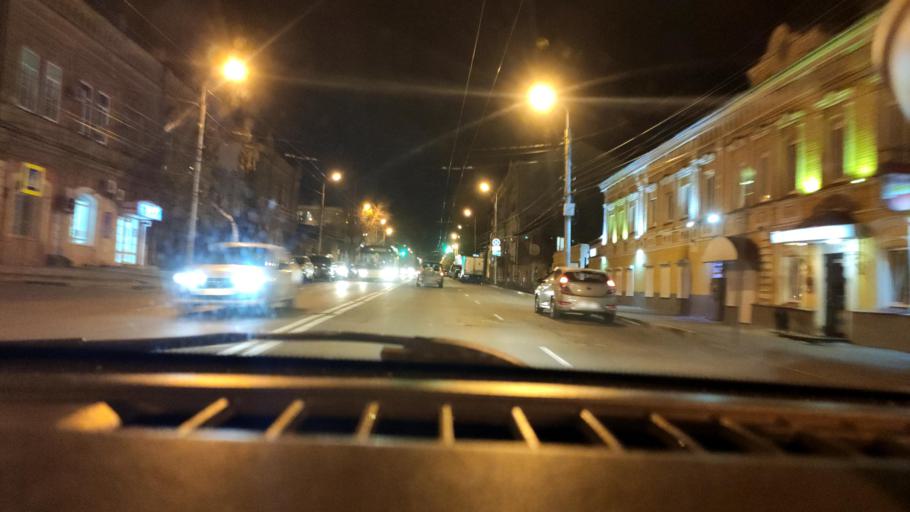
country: RU
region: Samara
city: Samara
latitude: 53.1861
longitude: 50.1008
